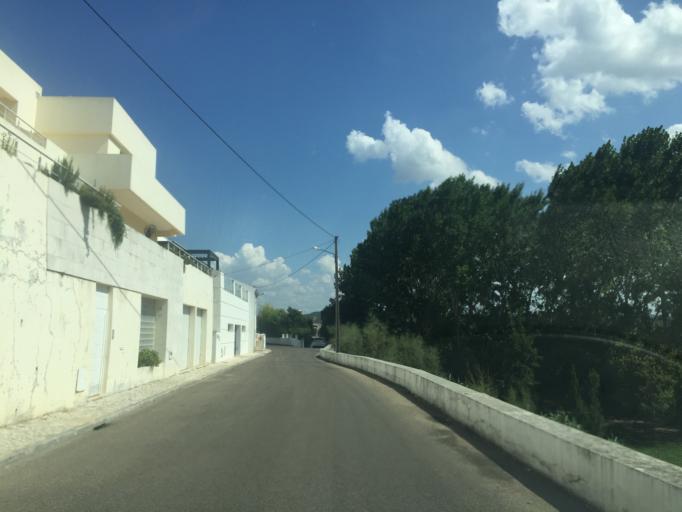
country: PT
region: Santarem
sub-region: Chamusca
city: Vila Nova da Barquinha
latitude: 39.4575
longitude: -8.4240
